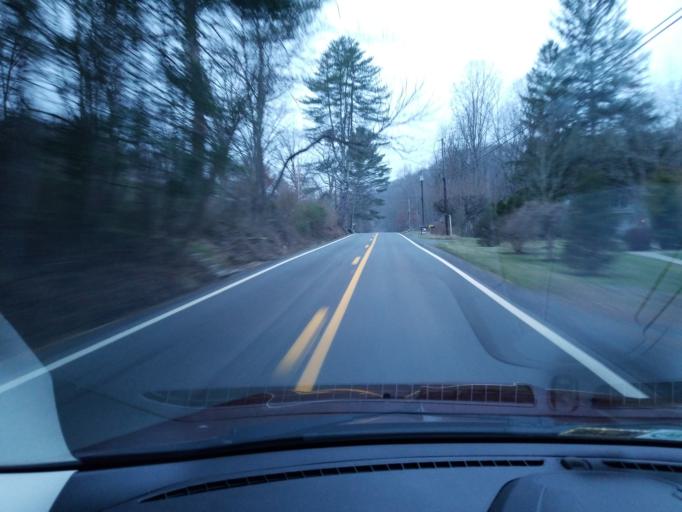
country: US
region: West Virginia
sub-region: Greenbrier County
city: Fairlea
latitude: 37.7562
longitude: -80.4003
